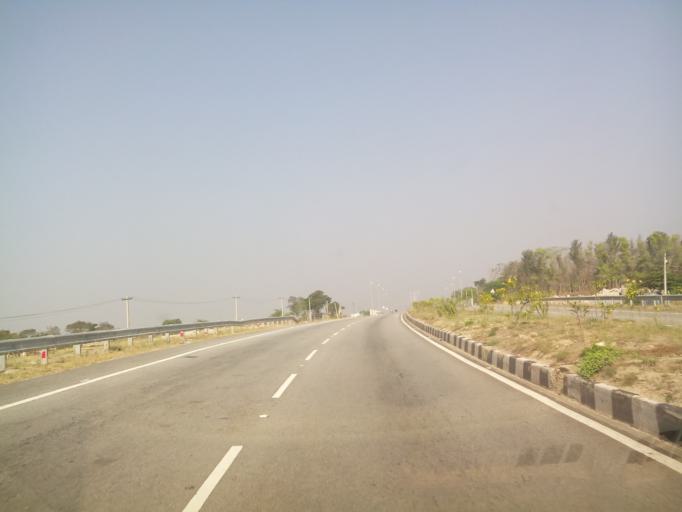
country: IN
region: Karnataka
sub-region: Tumkur
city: Kunigal
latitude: 13.0015
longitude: 76.9612
